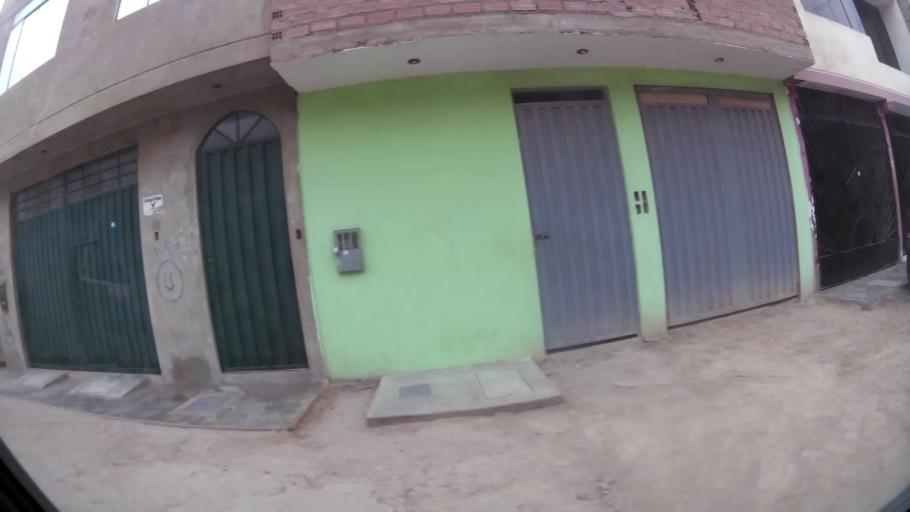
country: PE
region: Lima
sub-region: Lima
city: Independencia
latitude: -11.9633
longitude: -77.0939
